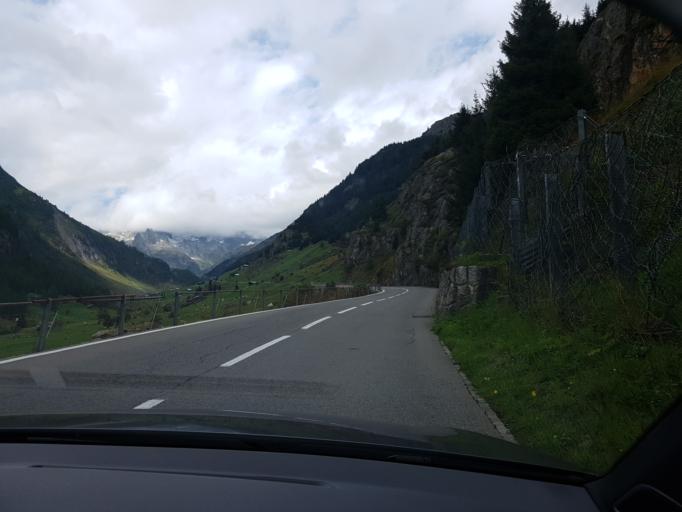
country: CH
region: Uri
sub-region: Uri
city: Andermatt
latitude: 46.7312
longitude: 8.5428
